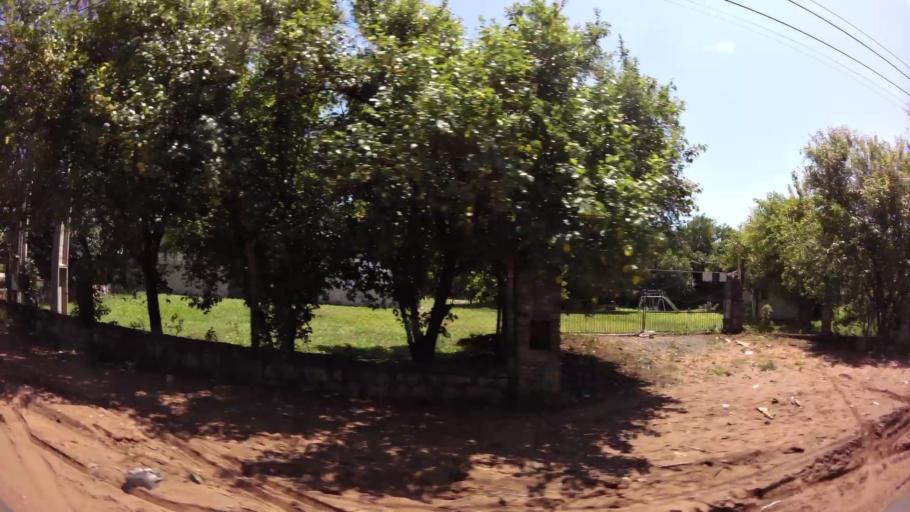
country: PY
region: Central
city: Nemby
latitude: -25.3977
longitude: -57.5331
